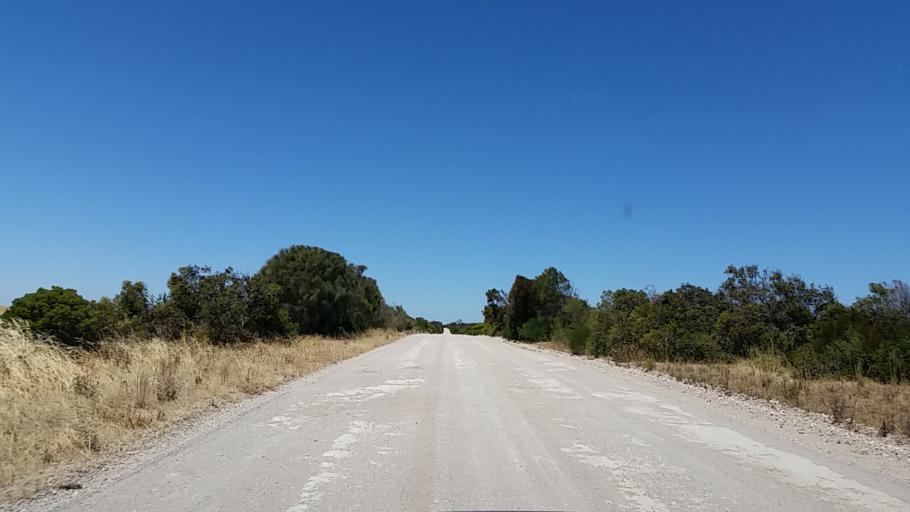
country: AU
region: South Australia
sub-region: Yorke Peninsula
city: Honiton
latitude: -35.0932
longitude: 137.4358
